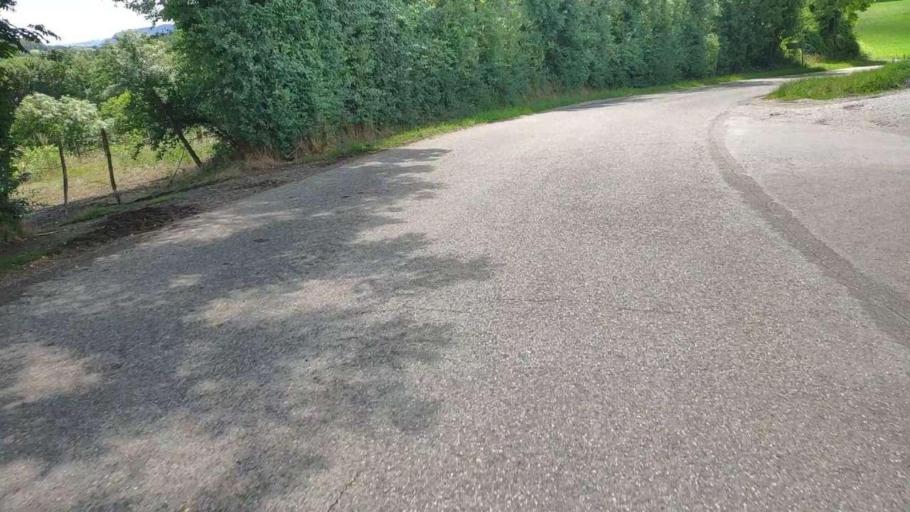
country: FR
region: Franche-Comte
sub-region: Departement du Jura
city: Poligny
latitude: 46.8258
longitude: 5.5684
